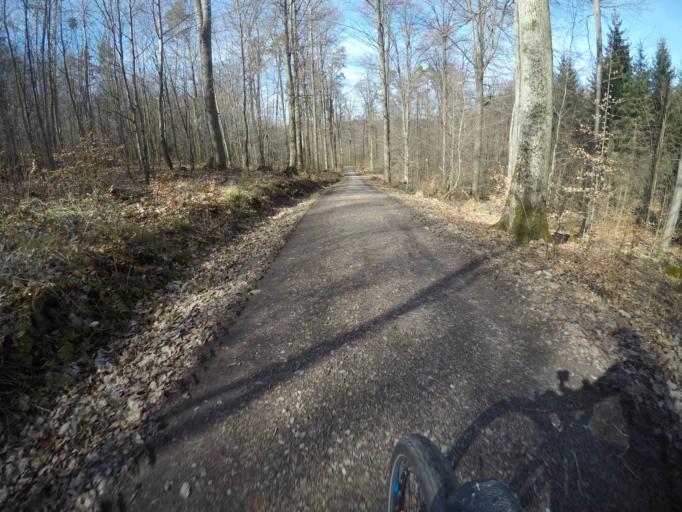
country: DE
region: Baden-Wuerttemberg
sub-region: Regierungsbezirk Stuttgart
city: Gerlingen
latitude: 48.7750
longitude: 9.0681
